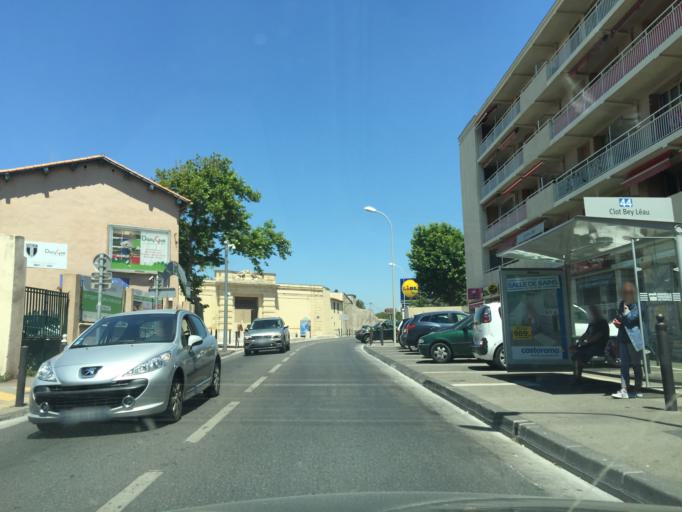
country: FR
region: Provence-Alpes-Cote d'Azur
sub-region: Departement des Bouches-du-Rhone
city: Marseille 08
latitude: 43.2559
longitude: 5.3823
